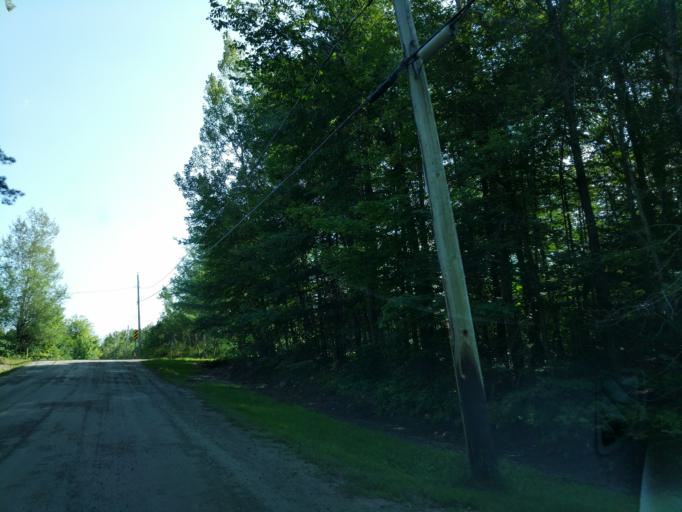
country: CA
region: Quebec
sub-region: Outaouais
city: Wakefield
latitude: 45.5069
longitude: -75.9537
